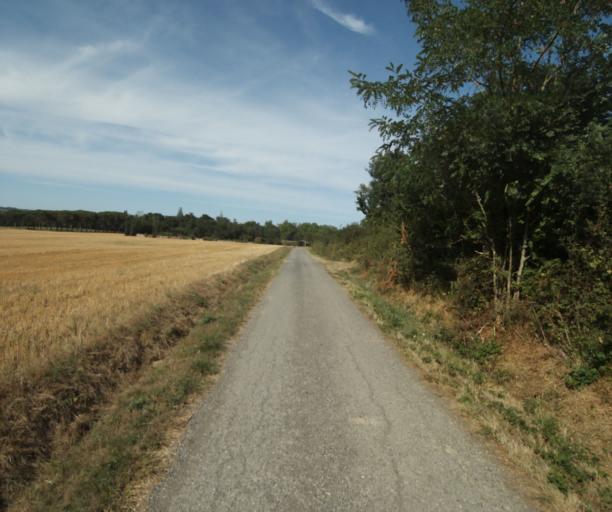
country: FR
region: Midi-Pyrenees
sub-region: Departement du Tarn
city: Soual
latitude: 43.5169
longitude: 2.0909
